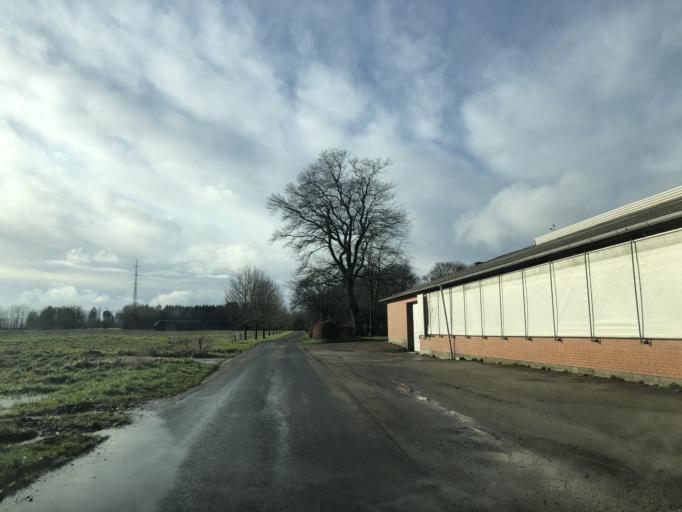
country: DK
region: North Denmark
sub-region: Vesthimmerland Kommune
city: Alestrup
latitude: 56.6405
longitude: 9.6202
